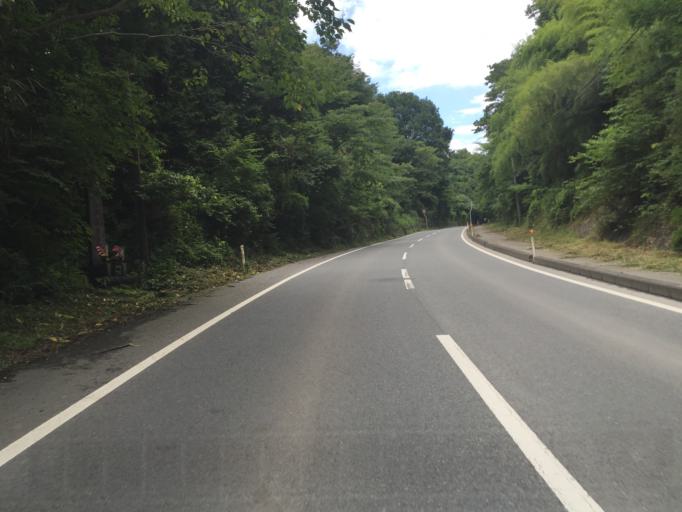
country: JP
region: Miyagi
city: Marumori
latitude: 37.7576
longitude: 140.9158
